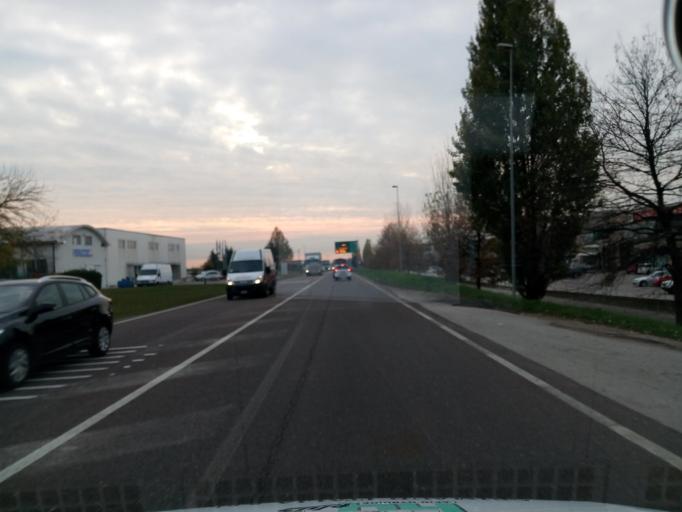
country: IT
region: Veneto
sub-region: Provincia di Vicenza
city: Thiene
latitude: 45.6923
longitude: 11.4659
